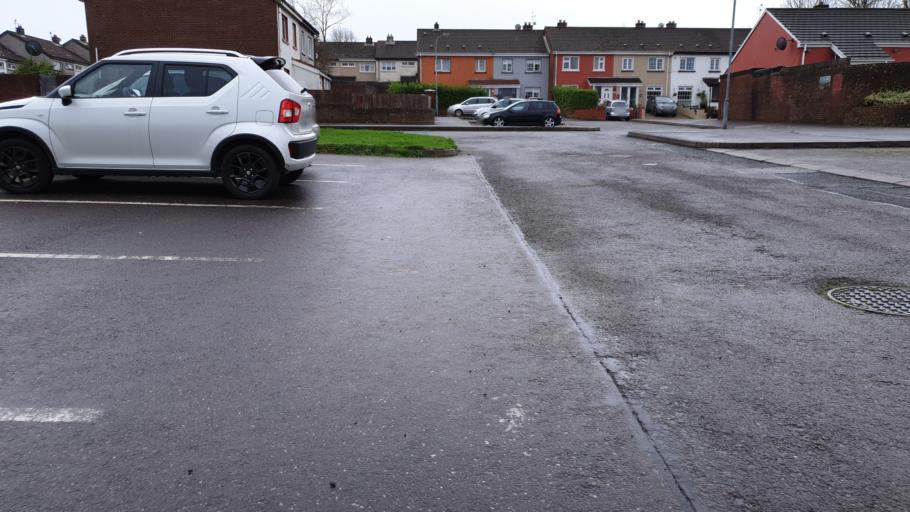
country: IE
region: Munster
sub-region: County Cork
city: Passage West
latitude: 51.8969
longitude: -8.4044
